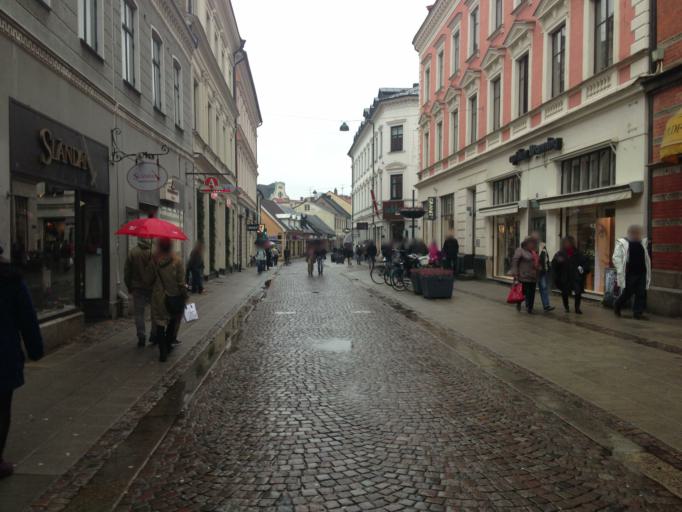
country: SE
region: Skane
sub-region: Lunds Kommun
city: Lund
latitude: 55.7033
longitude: 13.1919
